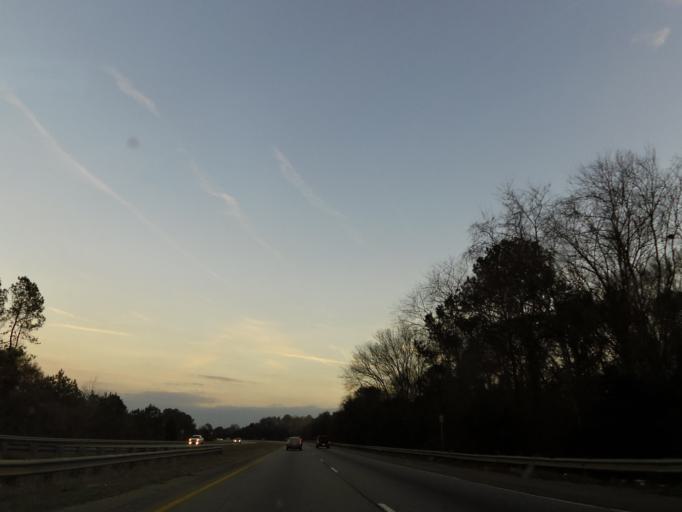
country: US
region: Georgia
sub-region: Dougherty County
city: Albany
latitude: 31.5973
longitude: -84.1412
